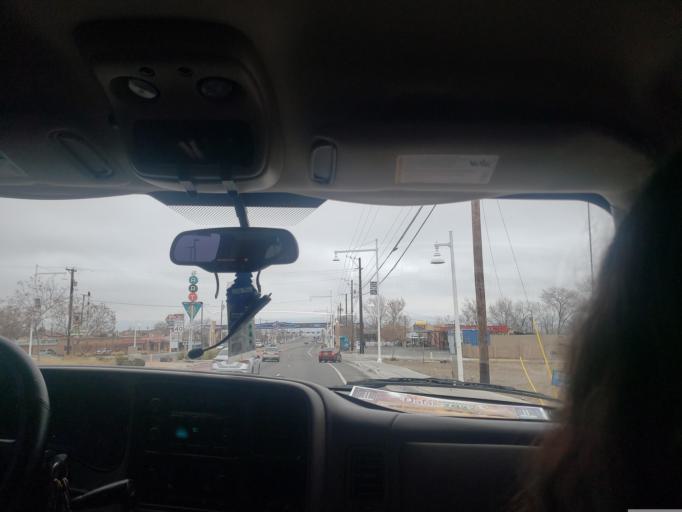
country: US
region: New Mexico
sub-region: Bernalillo County
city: Albuquerque
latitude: 35.0803
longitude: -106.7097
